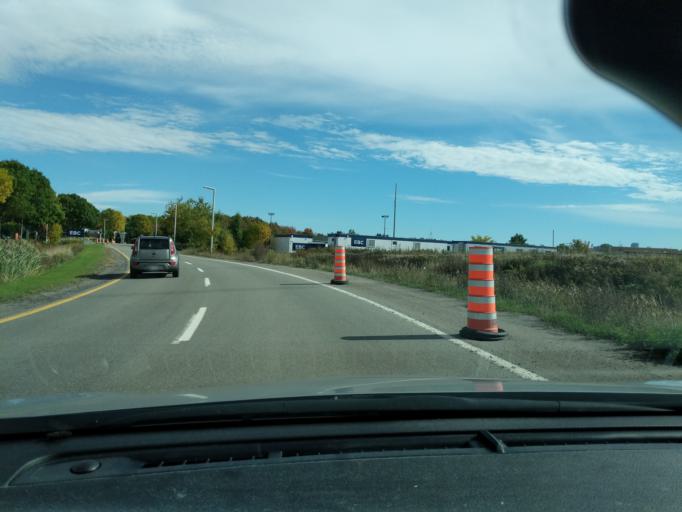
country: CA
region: Quebec
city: L'Ancienne-Lorette
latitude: 46.8011
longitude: -71.3225
